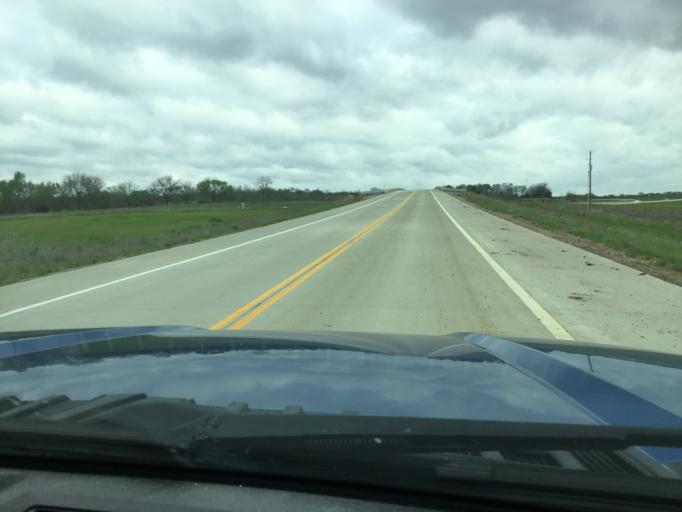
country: US
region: Kansas
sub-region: Douglas County
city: Lawrence
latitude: 38.9294
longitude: -95.1768
